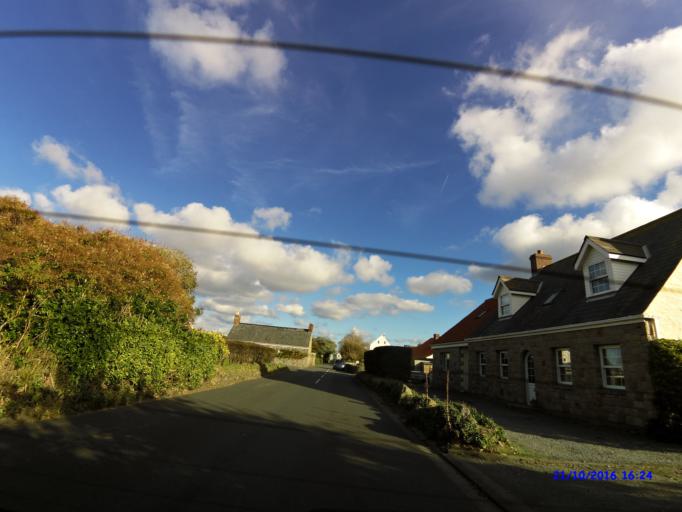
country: GG
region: St Peter Port
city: Saint Peter Port
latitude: 49.4628
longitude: -2.6289
